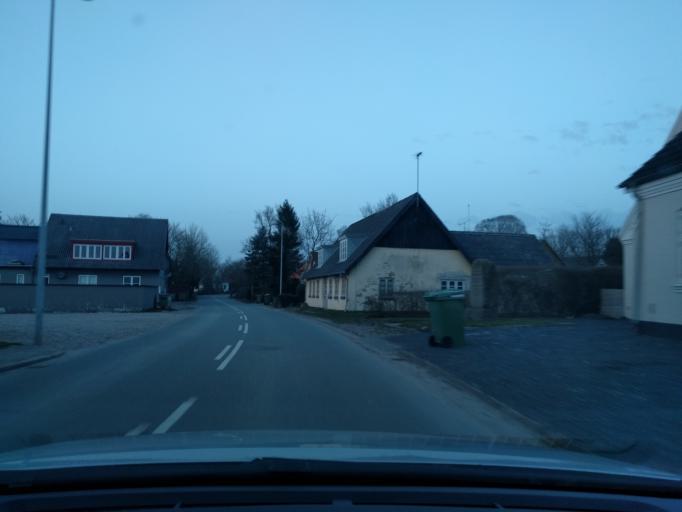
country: DK
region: South Denmark
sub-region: Odense Kommune
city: Bellinge
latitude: 55.3486
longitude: 10.2708
